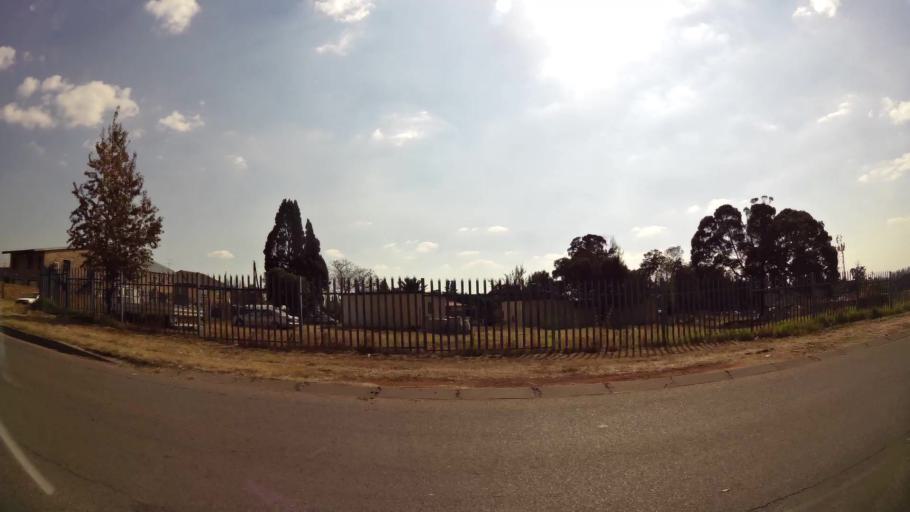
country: ZA
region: Gauteng
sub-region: City of Johannesburg Metropolitan Municipality
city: Modderfontein
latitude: -26.0919
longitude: 28.2550
